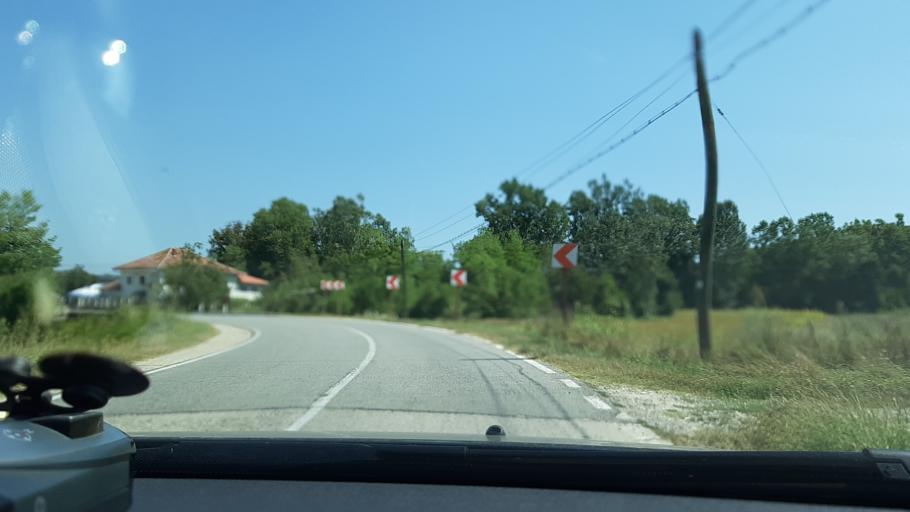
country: RO
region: Gorj
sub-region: Comuna Logresti-Mosteni
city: Logresti Mosteni
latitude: 44.8994
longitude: 23.7344
